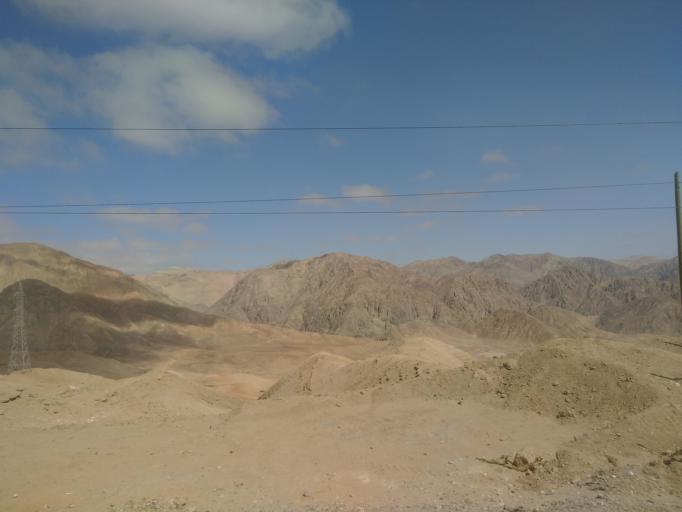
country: PE
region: Moquegua
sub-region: Provincia de Mariscal Nieto
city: Moquegua
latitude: -17.3912
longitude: -71.0149
